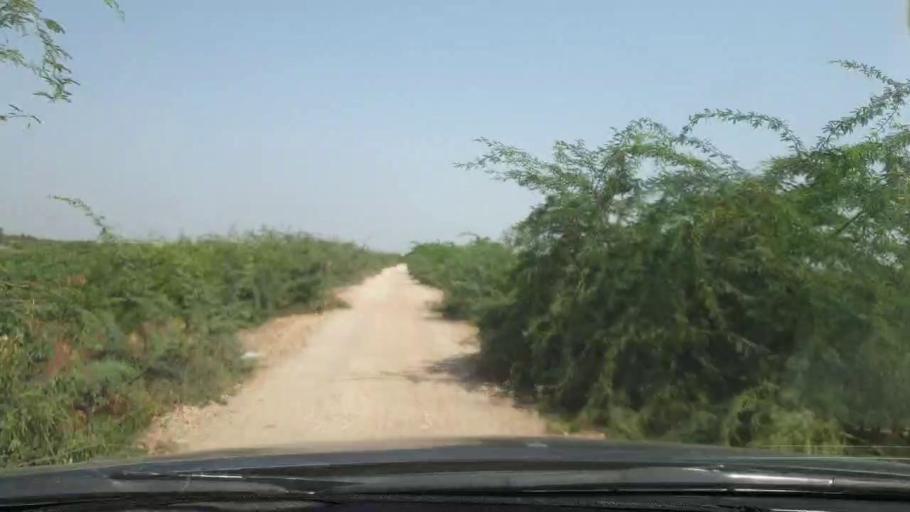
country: PK
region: Sindh
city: Naukot
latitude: 24.8132
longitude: 69.2578
